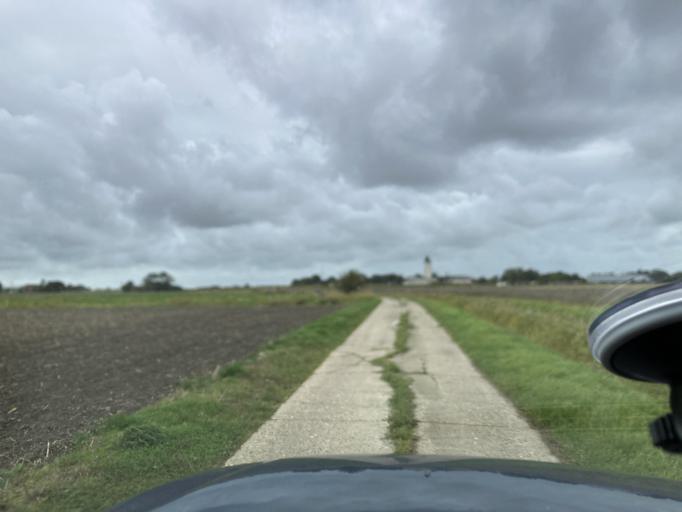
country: DE
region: Schleswig-Holstein
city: Norderwohrden
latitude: 54.2122
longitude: 9.0168
